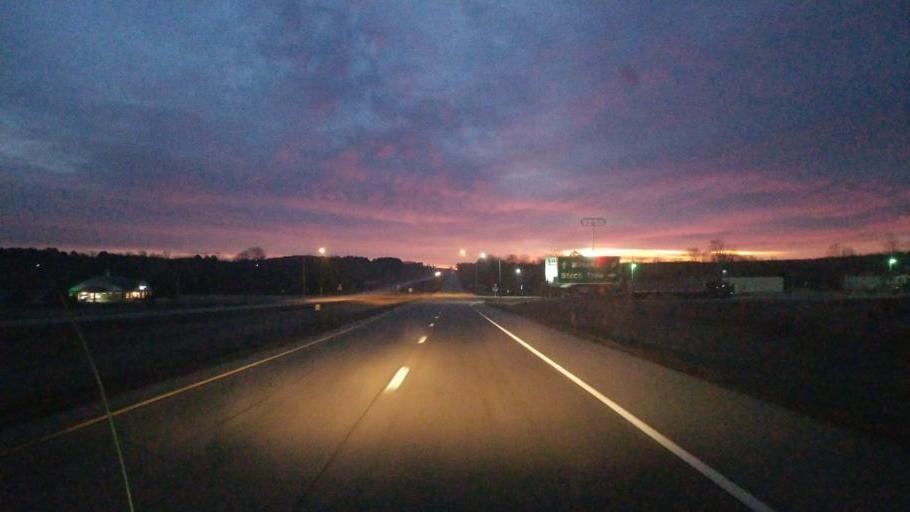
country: US
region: Missouri
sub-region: Shannon County
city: Winona
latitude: 36.9994
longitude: -91.4954
